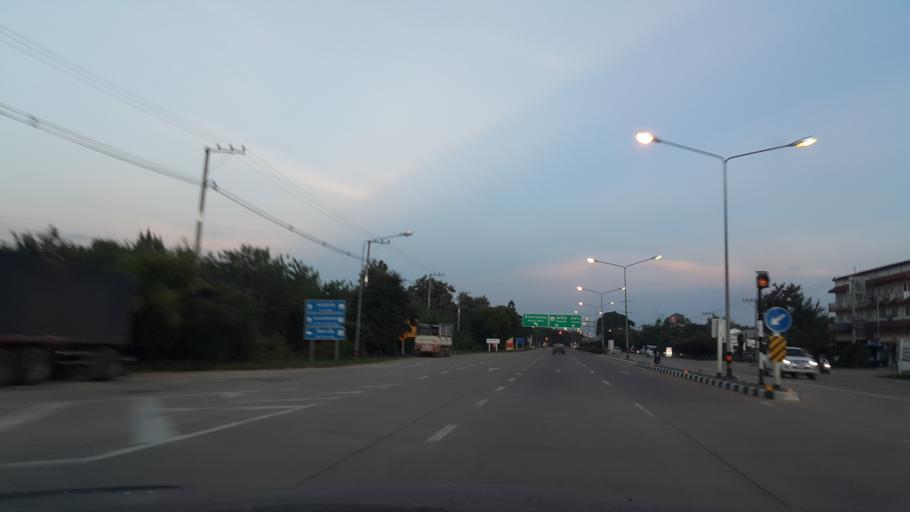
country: TH
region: Lamphun
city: Lamphun
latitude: 18.5726
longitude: 99.0144
